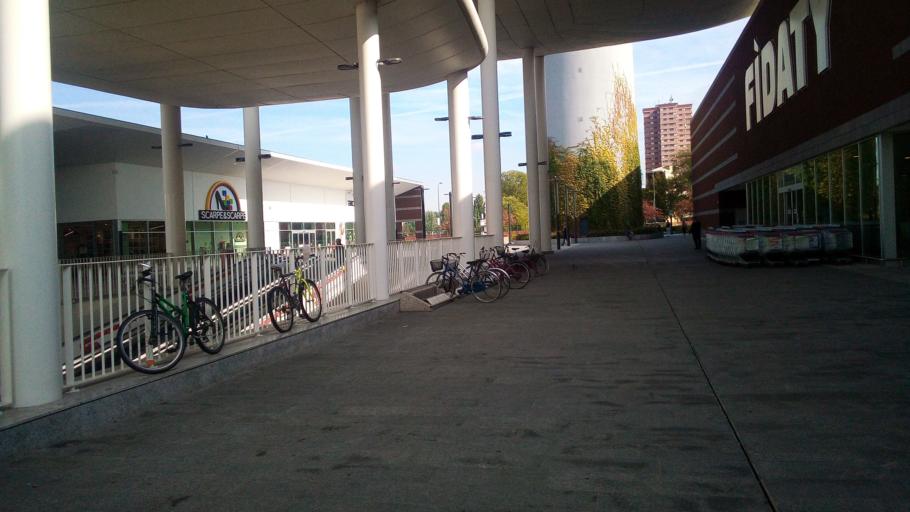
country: IT
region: Lombardy
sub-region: Citta metropolitana di Milano
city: Sesto San Giovanni
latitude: 45.5140
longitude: 9.2437
